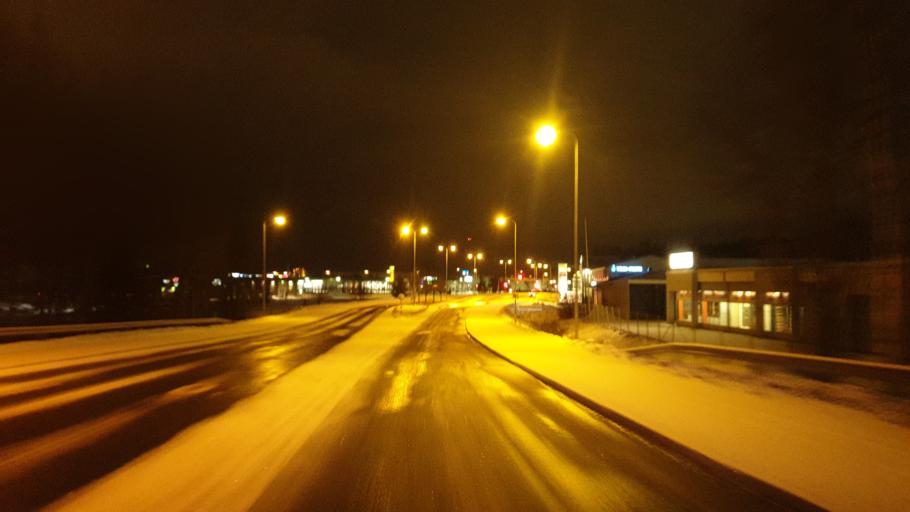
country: FI
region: Northern Ostrobothnia
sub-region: Oulu
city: Oulu
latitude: 64.9901
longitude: 25.4673
